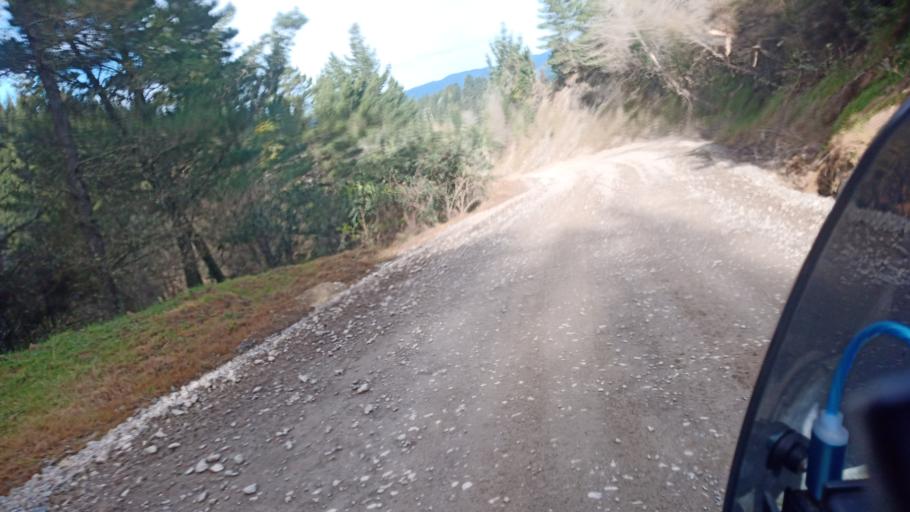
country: NZ
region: Gisborne
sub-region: Gisborne District
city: Gisborne
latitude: -38.1202
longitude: 178.1505
